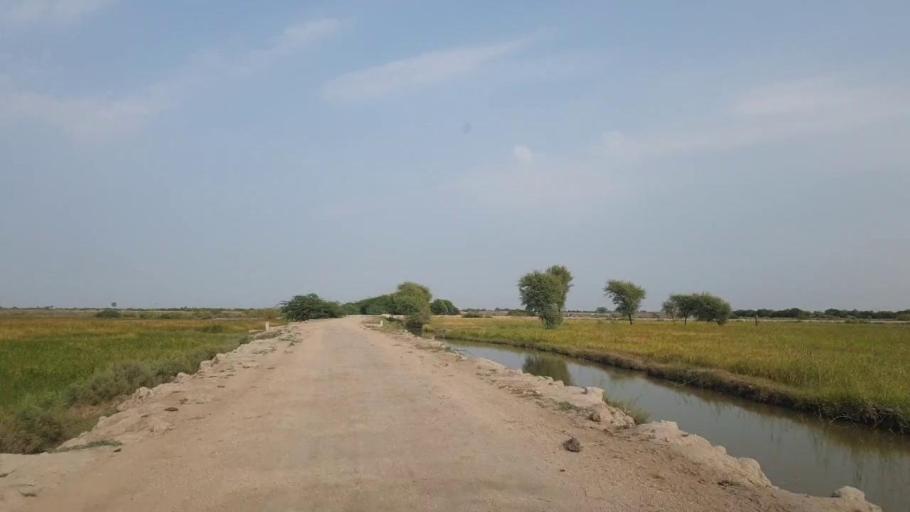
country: PK
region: Sindh
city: Kadhan
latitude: 24.4598
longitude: 68.8109
